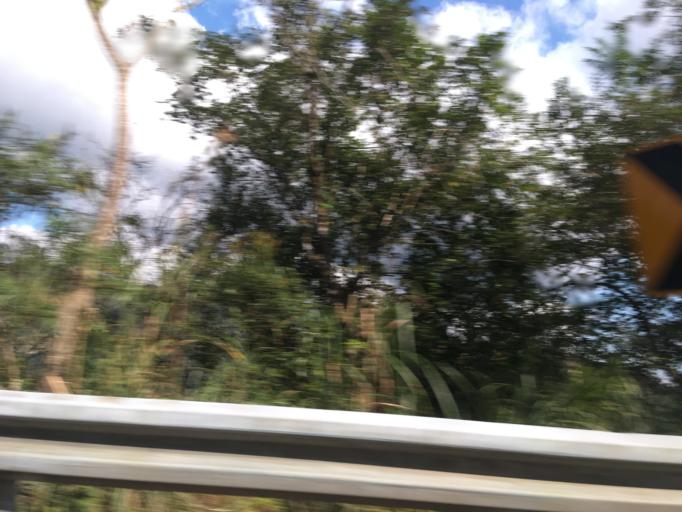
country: TW
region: Taiwan
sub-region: Yilan
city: Yilan
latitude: 24.7537
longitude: 121.6416
